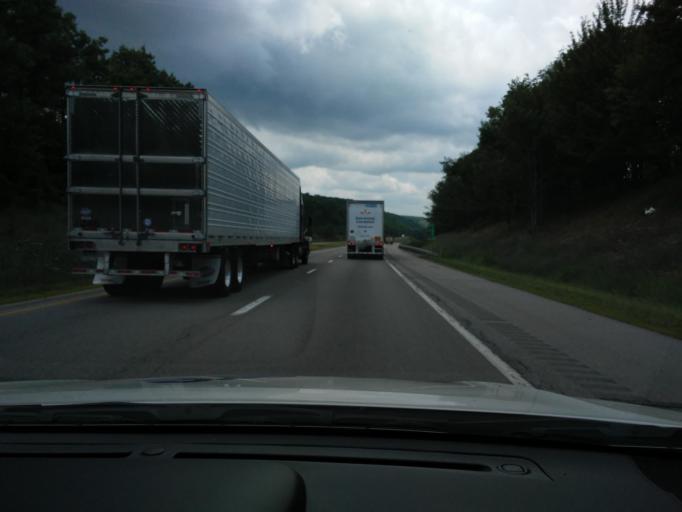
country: US
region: Pennsylvania
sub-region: Centre County
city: Milesburg
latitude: 41.0093
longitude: -77.9652
